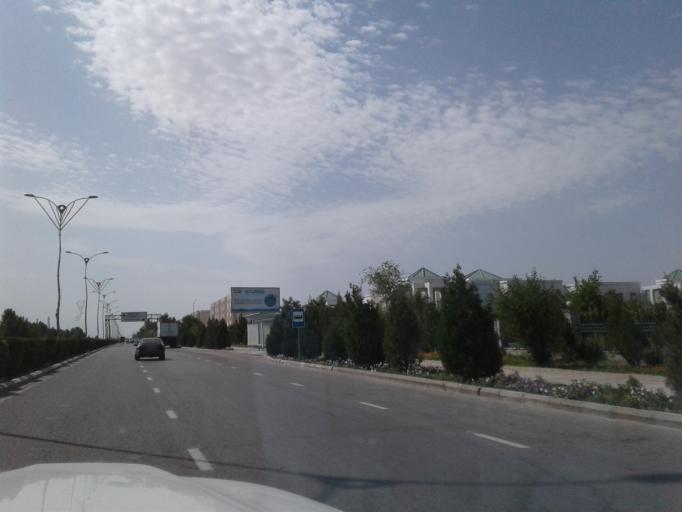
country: TM
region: Dasoguz
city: Dasoguz
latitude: 41.8346
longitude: 59.9320
